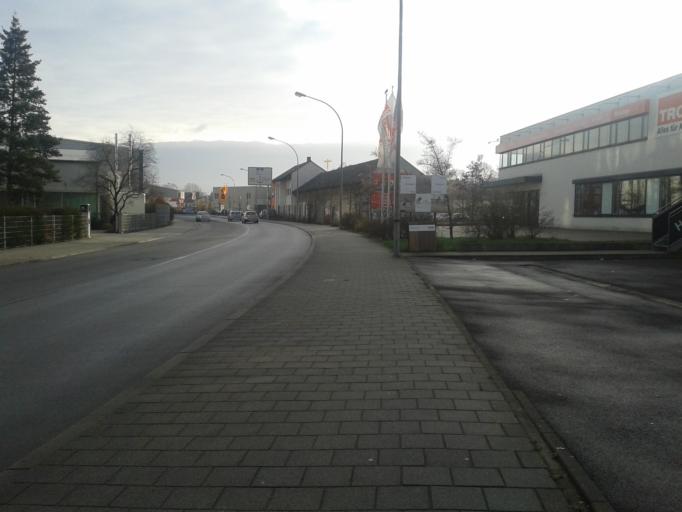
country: DE
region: Bavaria
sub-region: Upper Franconia
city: Hallstadt
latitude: 49.9078
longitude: 10.8806
